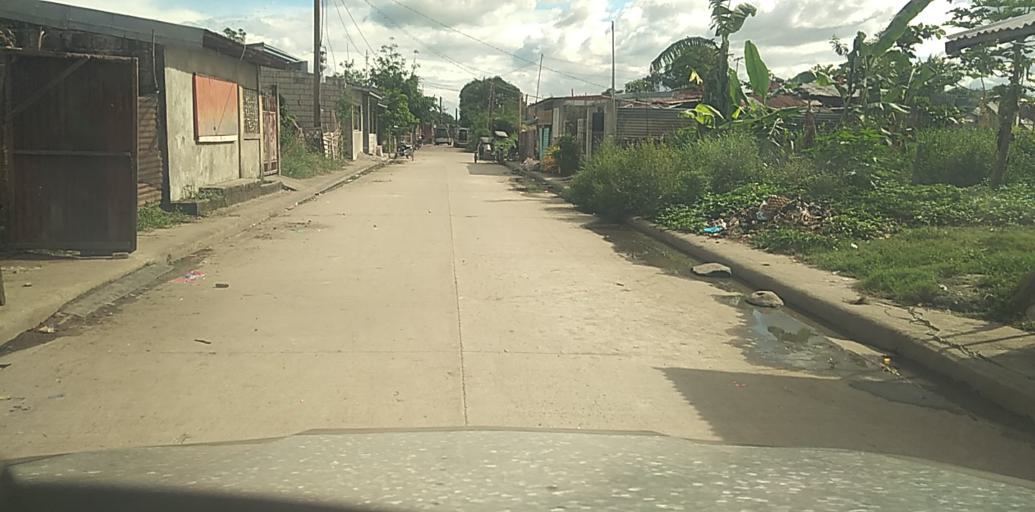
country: PH
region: Central Luzon
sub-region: Province of Pampanga
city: Buensuseso
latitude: 15.1807
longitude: 120.6683
